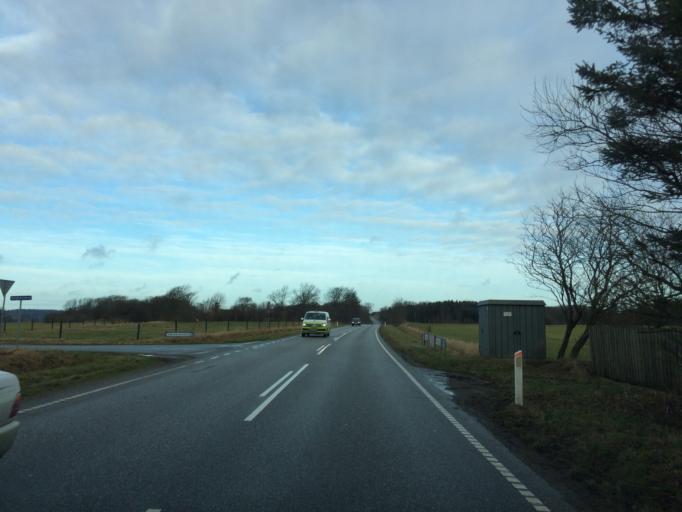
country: DK
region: Central Jutland
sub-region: Struer Kommune
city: Struer
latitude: 56.4740
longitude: 8.5495
